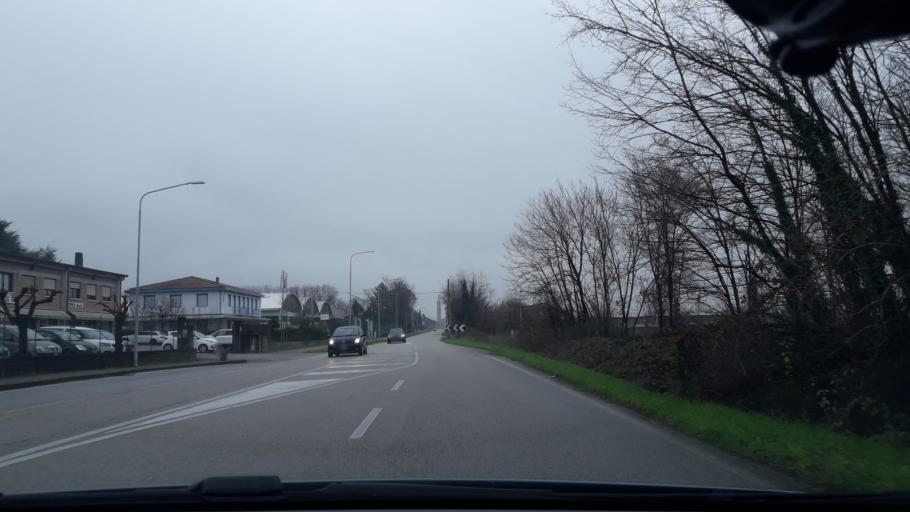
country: IT
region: Friuli Venezia Giulia
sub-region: Provincia di Udine
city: Pasian di Prato
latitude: 46.0516
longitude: 13.1724
